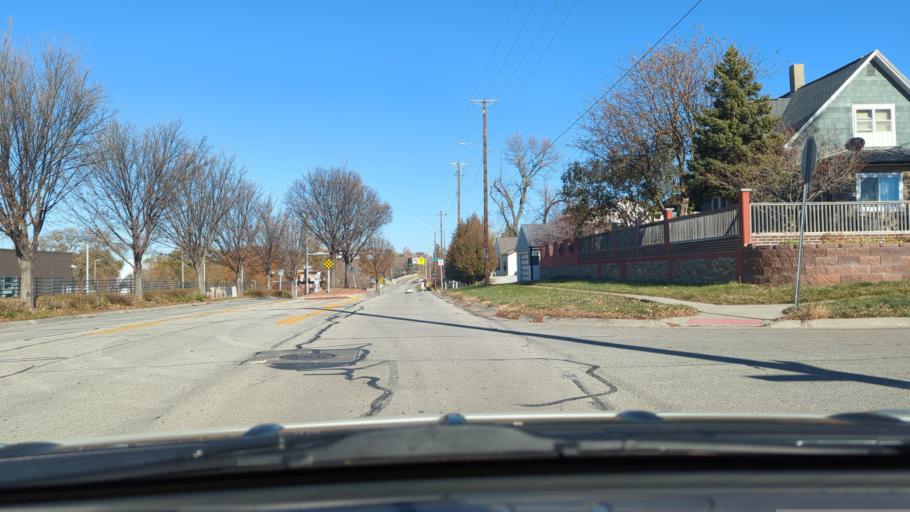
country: US
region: Nebraska
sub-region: Sarpy County
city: La Vista
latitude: 41.2008
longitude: -95.9770
